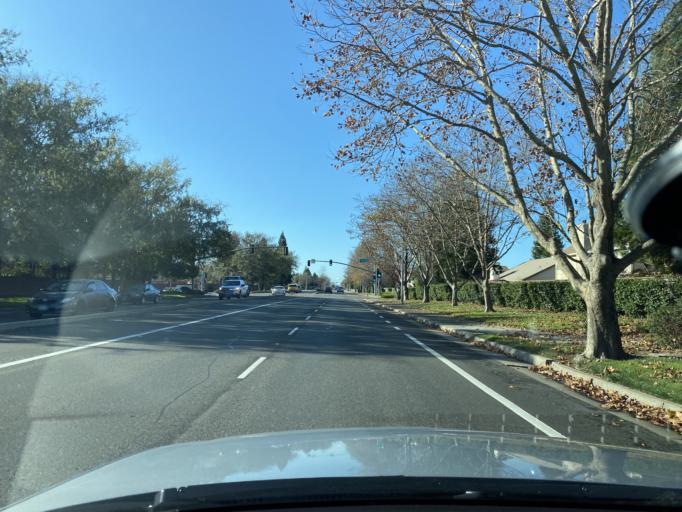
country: US
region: California
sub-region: Sacramento County
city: Elk Grove
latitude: 38.4381
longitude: -121.3786
